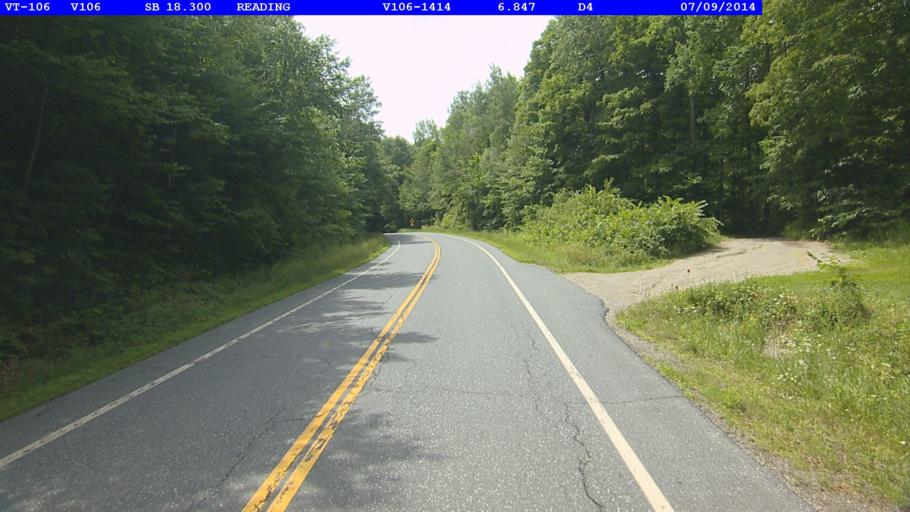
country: US
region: Vermont
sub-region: Windsor County
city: Woodstock
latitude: 43.5329
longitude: -72.5557
